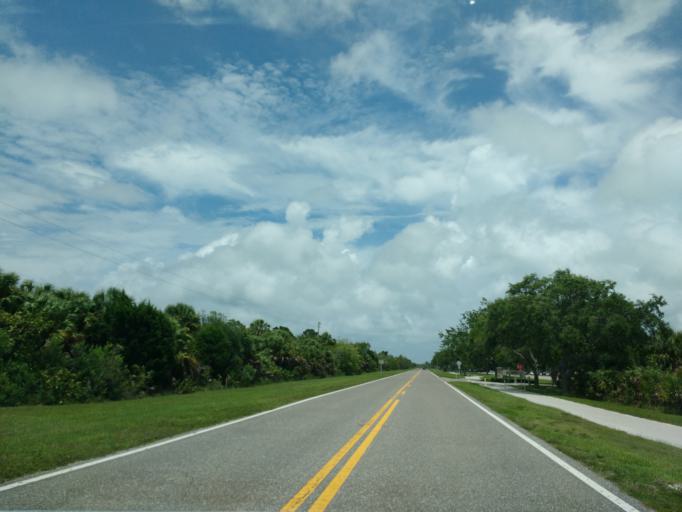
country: US
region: Florida
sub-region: Pinellas County
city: Tierra Verde
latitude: 27.6247
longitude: -82.7122
